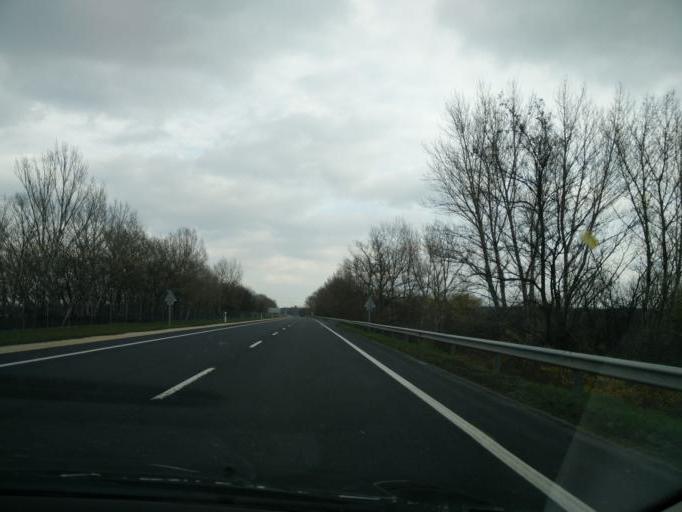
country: HU
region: Gyor-Moson-Sopron
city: Per
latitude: 47.6929
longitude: 17.7888
